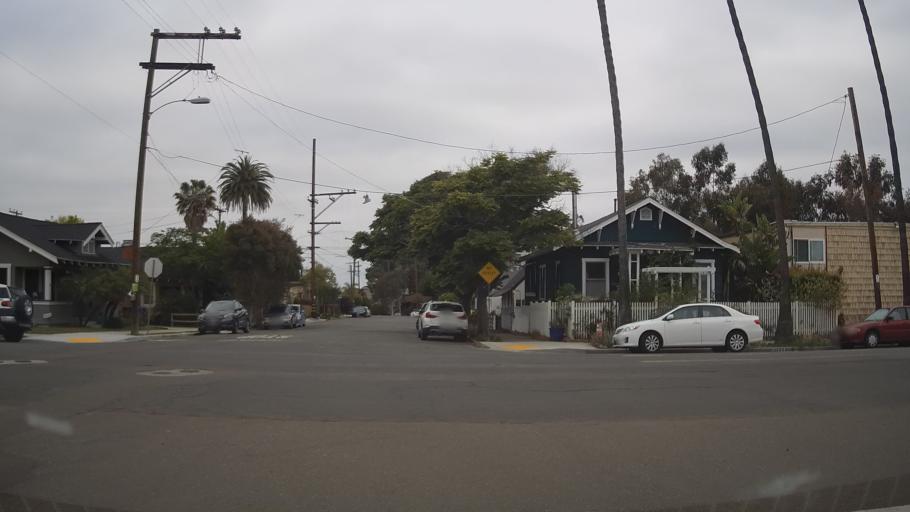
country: US
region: California
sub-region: San Diego County
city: San Diego
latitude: 32.7591
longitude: -117.1510
